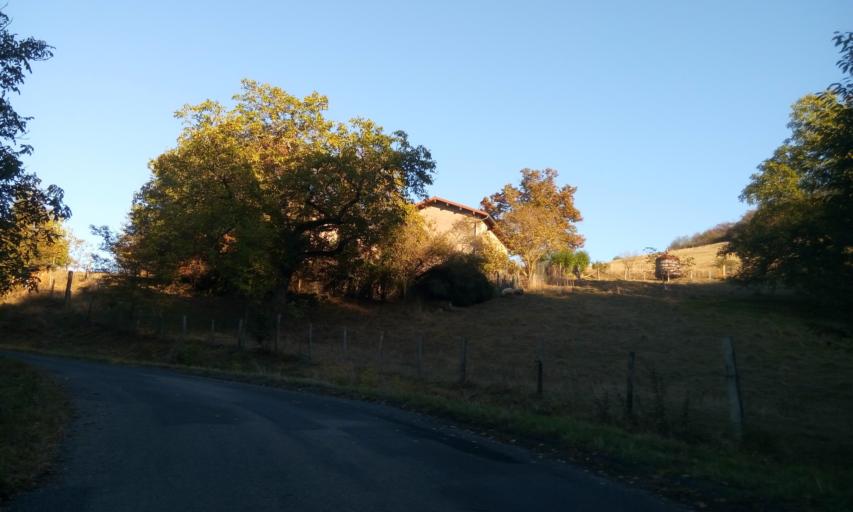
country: FR
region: Rhone-Alpes
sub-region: Departement du Rhone
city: Tarare
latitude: 45.9154
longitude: 4.4475
